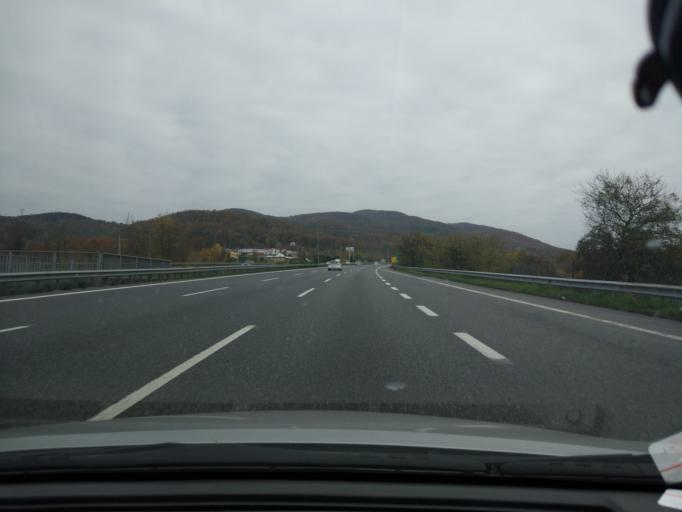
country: TR
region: Sakarya
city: Karadere
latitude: 40.8043
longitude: 30.8536
